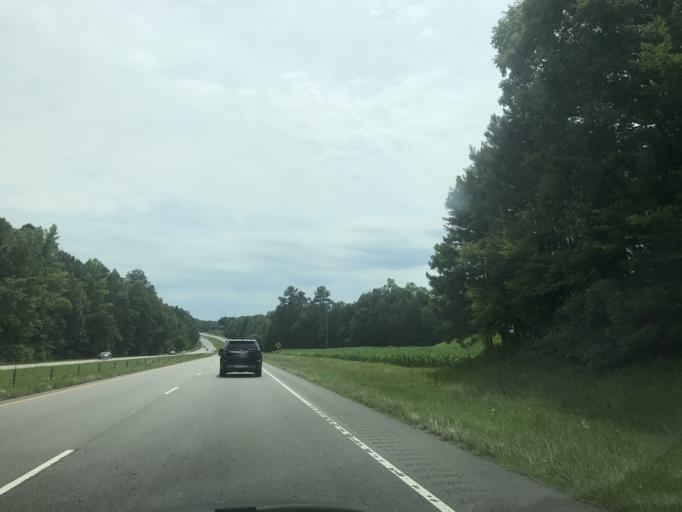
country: US
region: North Carolina
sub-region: Vance County
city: South Henderson
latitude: 36.2563
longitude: -78.4268
